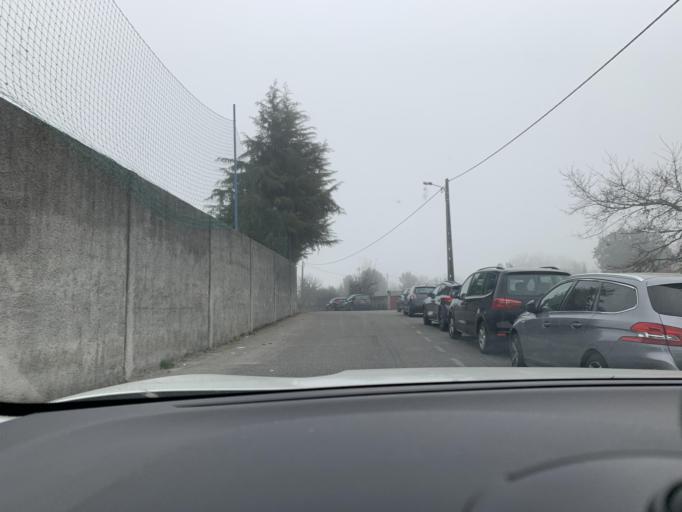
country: PT
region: Viseu
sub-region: Viseu
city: Viseu
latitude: 40.6341
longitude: -7.9198
